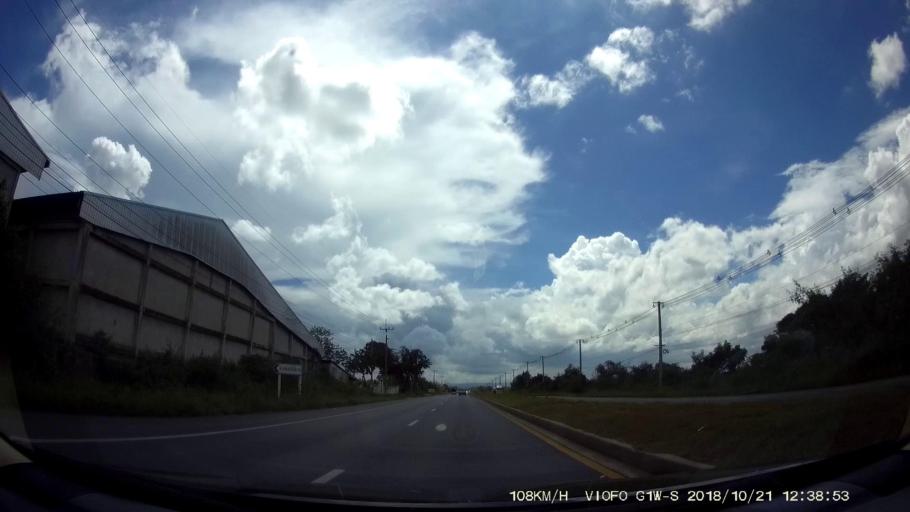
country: TH
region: Nakhon Ratchasima
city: Amphoe Sikhiu
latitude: 15.0471
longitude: 101.7036
